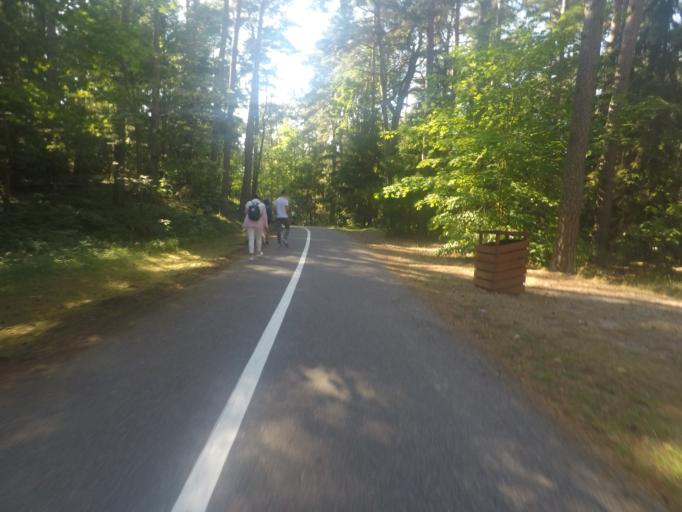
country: LT
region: Klaipedos apskritis
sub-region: Klaipeda
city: Klaipeda
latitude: 55.5452
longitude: 21.1172
